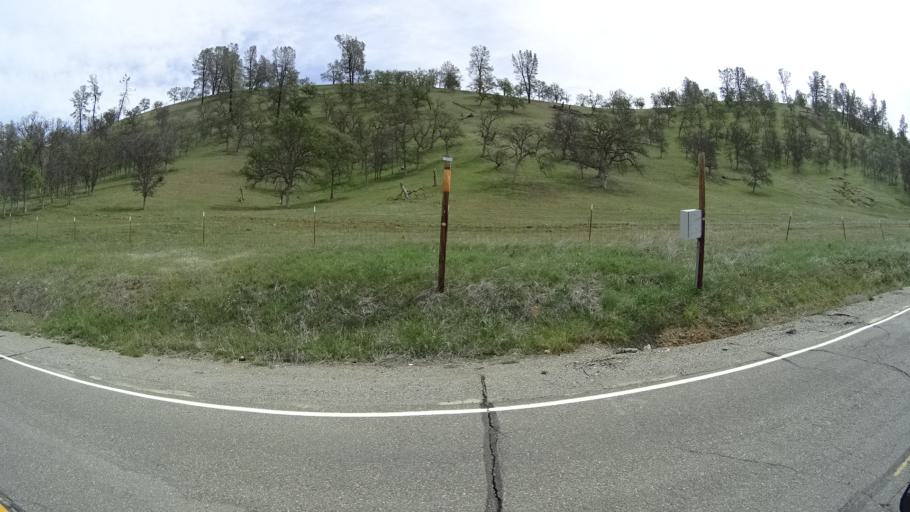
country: US
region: California
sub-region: Glenn County
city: Willows
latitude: 39.5684
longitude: -122.5406
